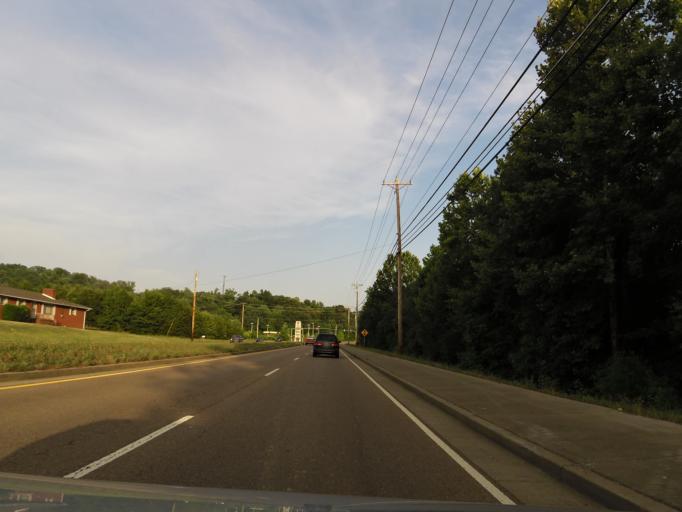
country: US
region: Tennessee
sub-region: Knox County
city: Farragut
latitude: 35.9497
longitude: -84.1165
